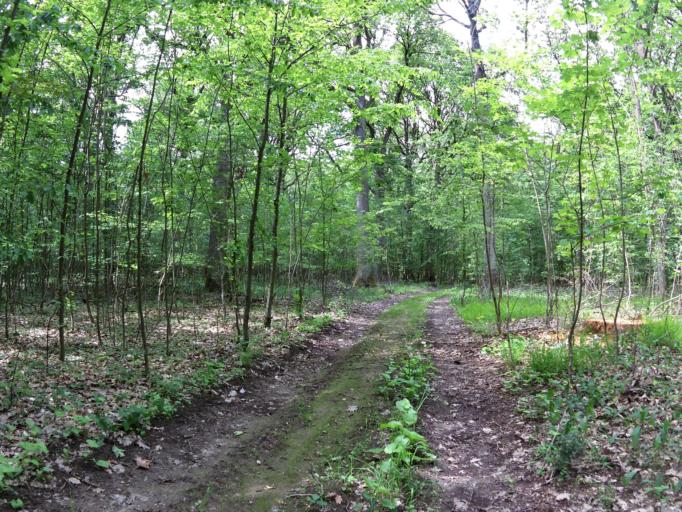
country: DE
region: Bavaria
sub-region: Regierungsbezirk Unterfranken
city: Theilheim
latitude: 49.7313
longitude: 10.0540
